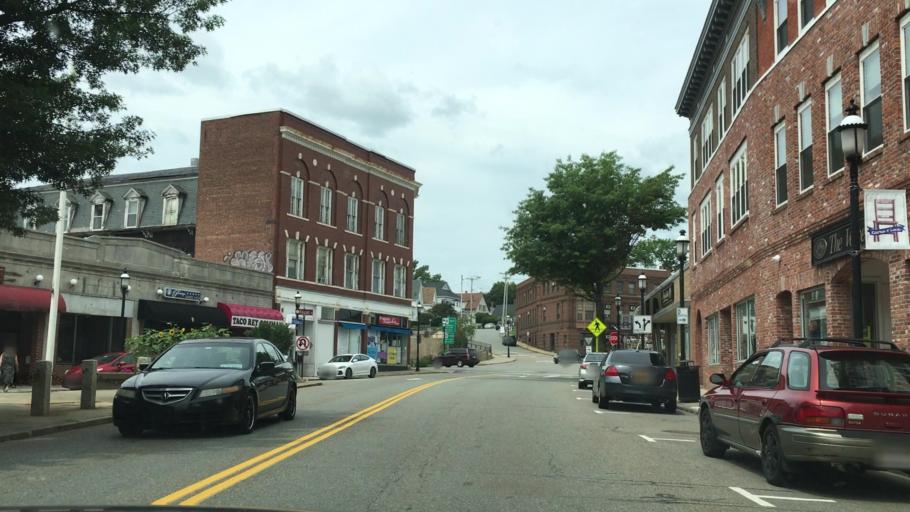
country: US
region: Massachusetts
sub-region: Worcester County
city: Gardner
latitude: 42.5753
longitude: -71.9949
